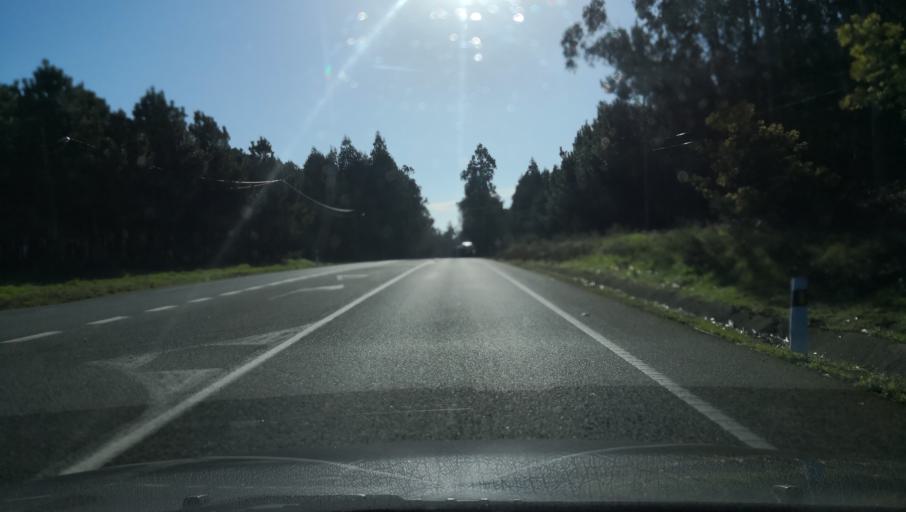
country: ES
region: Galicia
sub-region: Provincia da Coruna
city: Vedra
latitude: 42.7938
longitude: -8.4618
